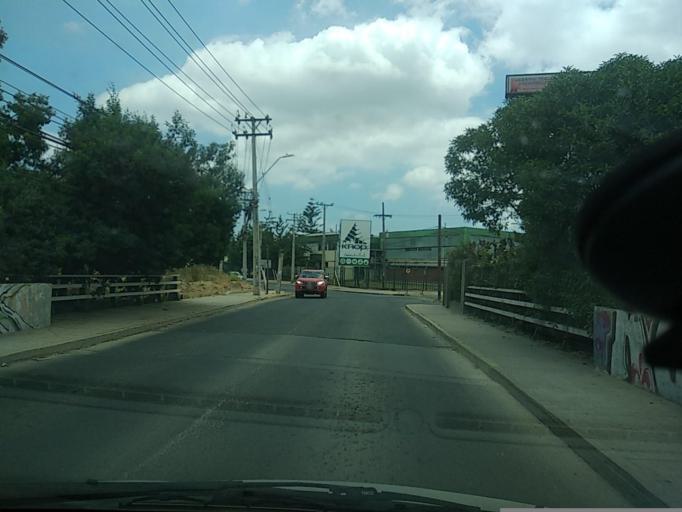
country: CL
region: Valparaiso
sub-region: Provincia de Marga Marga
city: Quilpue
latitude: -33.0414
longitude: -71.4119
